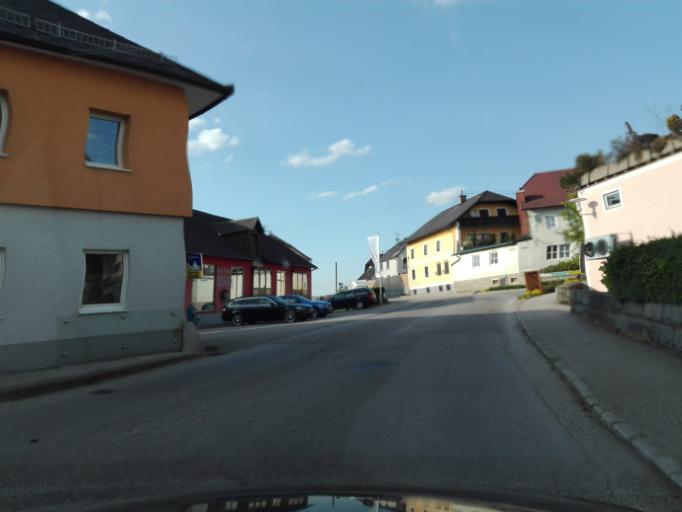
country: AT
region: Upper Austria
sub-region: Politischer Bezirk Rohrbach
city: Kleinzell im Muehlkreis
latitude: 48.4853
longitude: 13.9681
